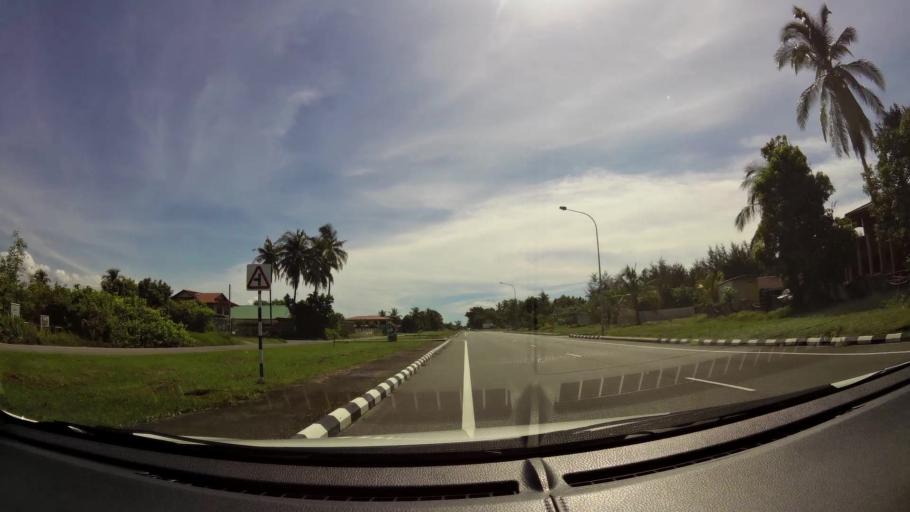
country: BN
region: Belait
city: Kuala Belait
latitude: 4.5903
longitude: 114.2146
